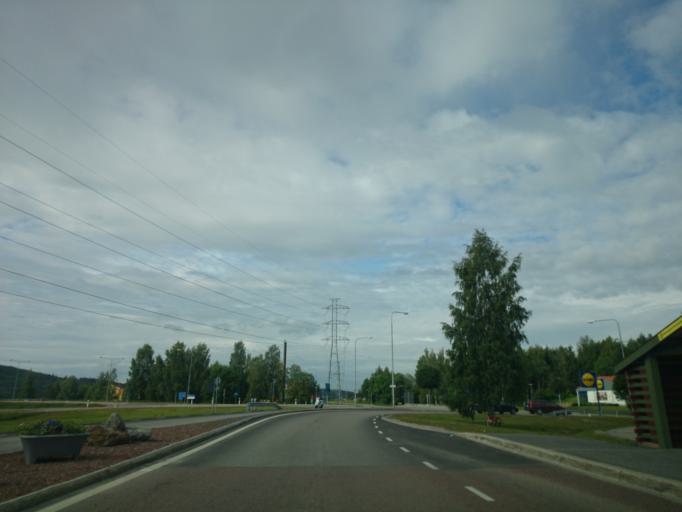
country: SE
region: Vaesternorrland
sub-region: Timra Kommun
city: Timra
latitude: 62.4820
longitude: 17.3149
